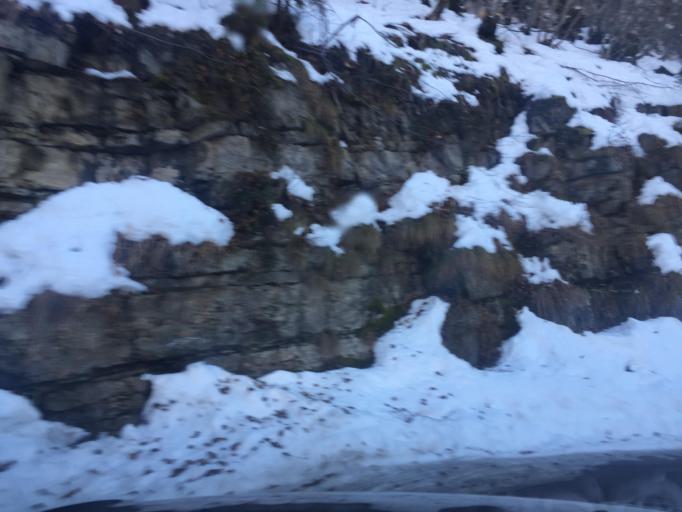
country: IT
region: Friuli Venezia Giulia
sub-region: Provincia di Udine
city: Lauco
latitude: 46.4348
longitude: 12.9703
